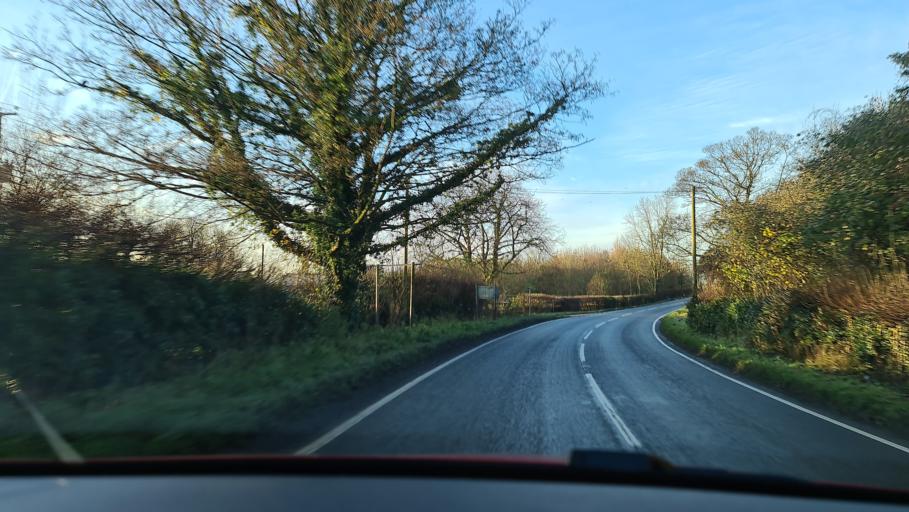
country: GB
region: England
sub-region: Buckinghamshire
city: Waddesdon
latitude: 51.8259
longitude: -0.9114
